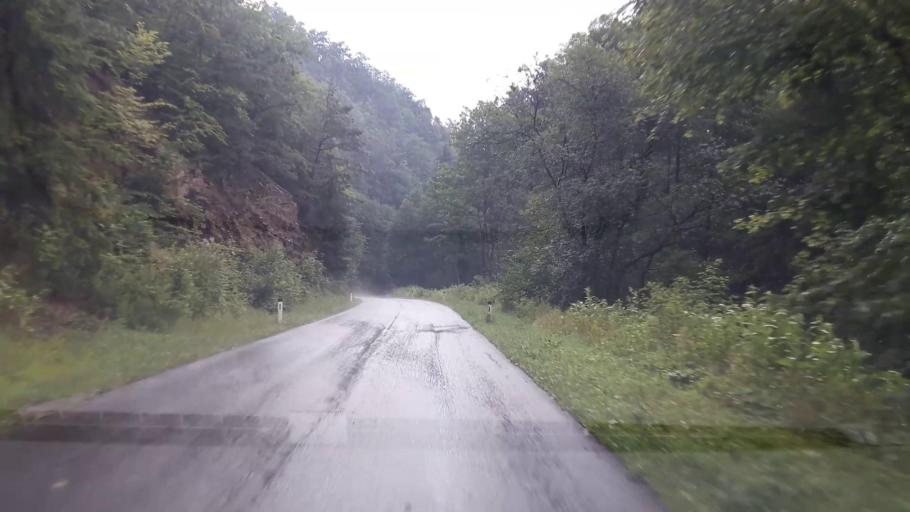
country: AT
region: Lower Austria
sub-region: Politischer Bezirk Krems
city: Aggsbach
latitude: 48.2884
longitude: 15.3833
